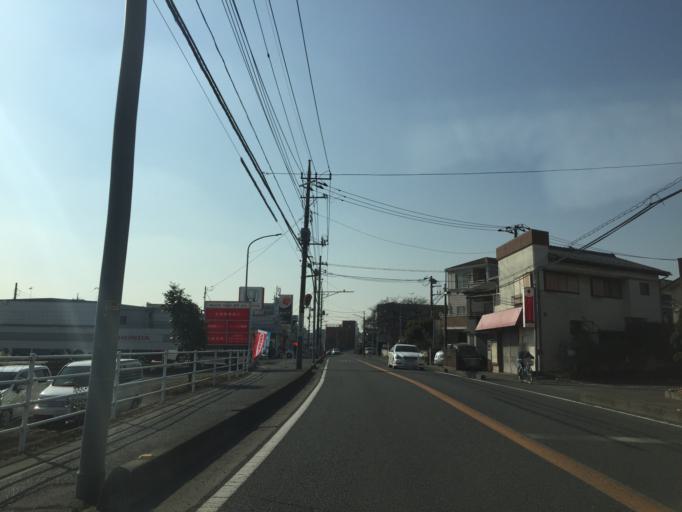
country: JP
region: Saitama
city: Shiki
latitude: 35.8414
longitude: 139.5832
